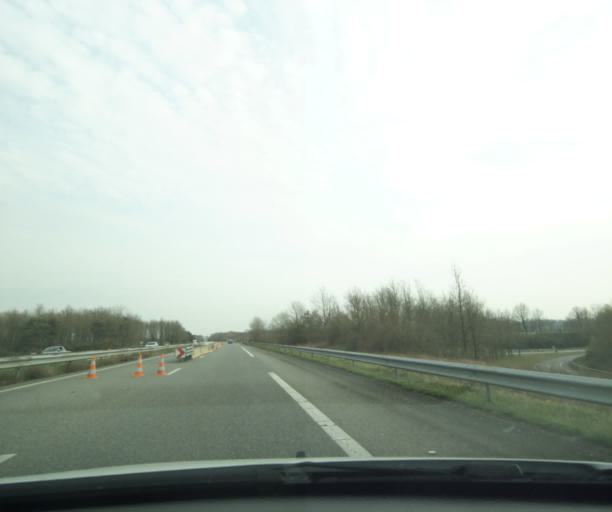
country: FR
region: Aquitaine
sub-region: Departement des Pyrenees-Atlantiques
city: Artix
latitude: 43.3976
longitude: -0.5496
